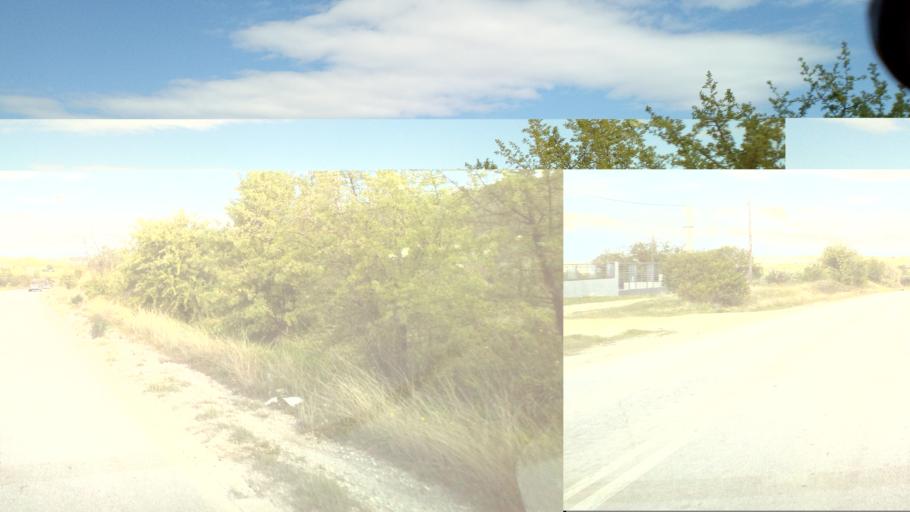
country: GR
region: Central Macedonia
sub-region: Nomos Kilkis
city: Nea Santa
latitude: 40.8255
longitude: 22.9243
